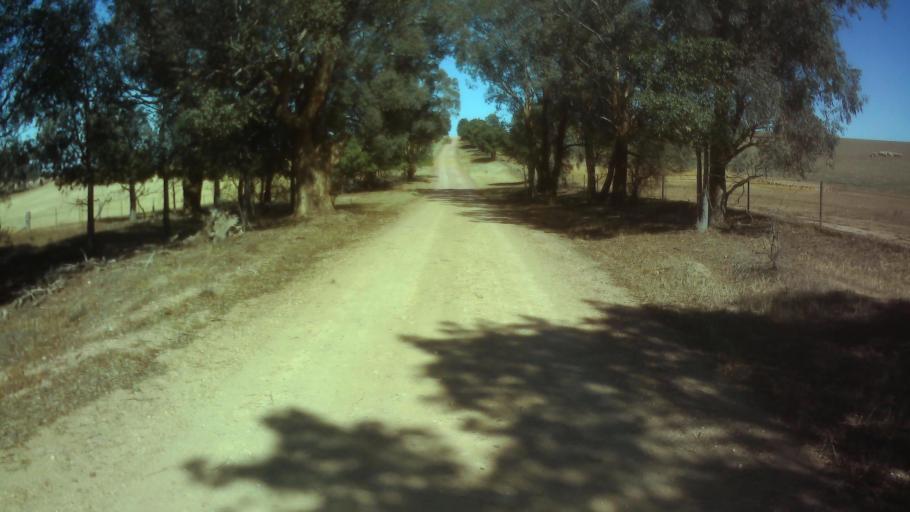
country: AU
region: New South Wales
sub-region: Weddin
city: Grenfell
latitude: -33.9932
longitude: 148.3506
